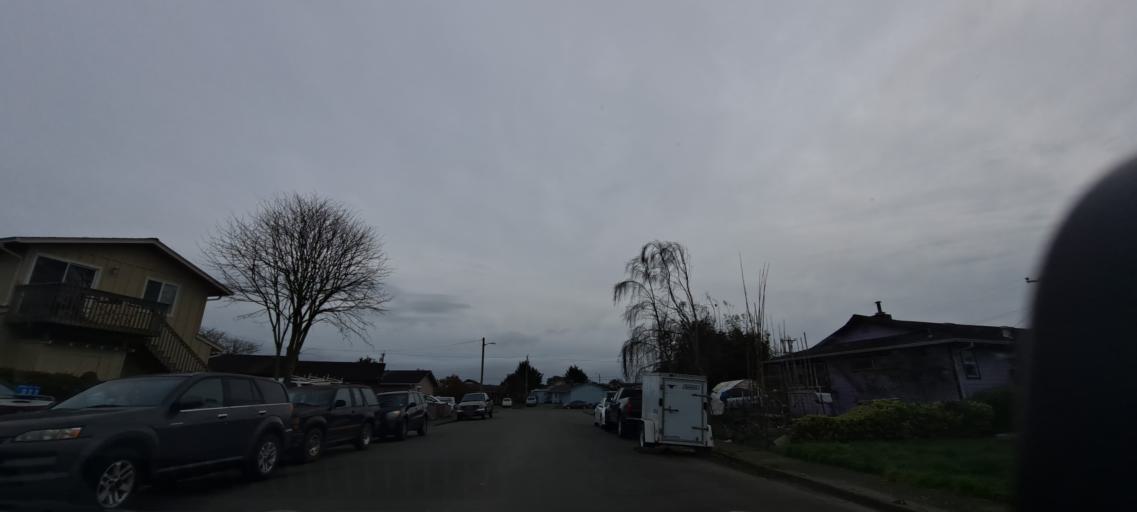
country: US
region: California
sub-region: Humboldt County
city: Arcata
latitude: 40.8732
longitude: -124.1051
